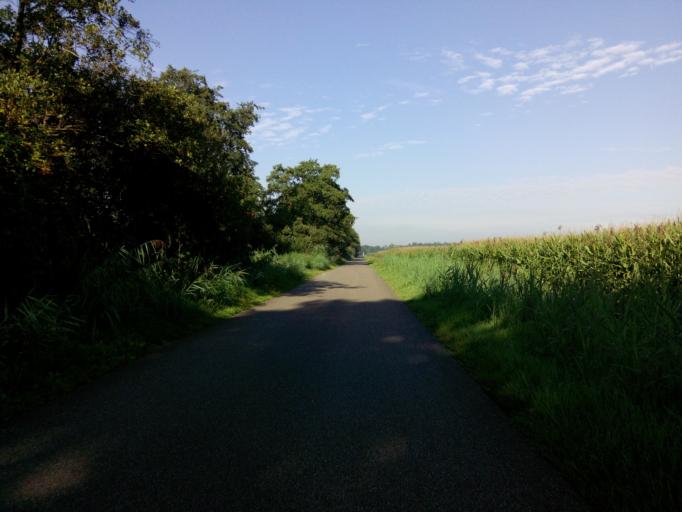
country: NL
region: Utrecht
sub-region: Gemeente Utrechtse Heuvelrug
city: Overberg
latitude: 52.0521
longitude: 5.4640
